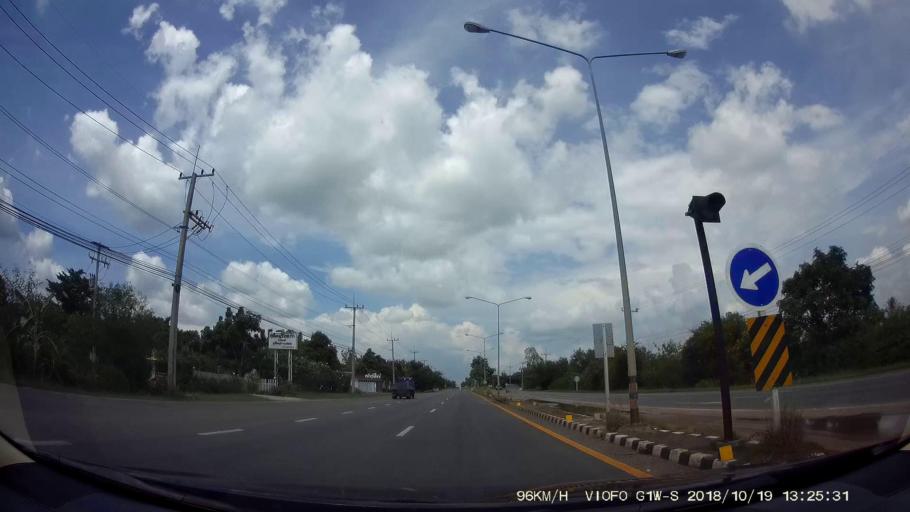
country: TH
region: Chaiyaphum
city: Chatturat
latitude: 15.5224
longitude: 101.8265
